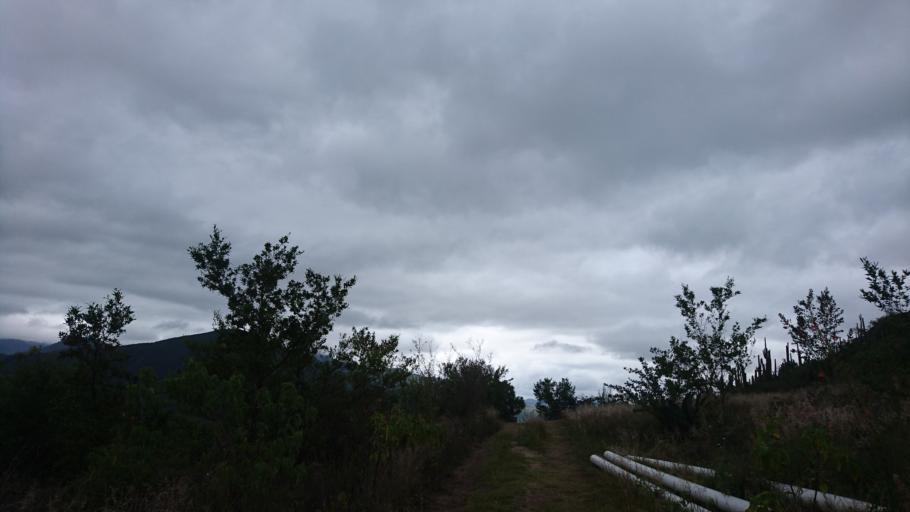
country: MX
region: Oaxaca
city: San Lorenzo Albarradas
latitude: 16.8679
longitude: -96.2752
